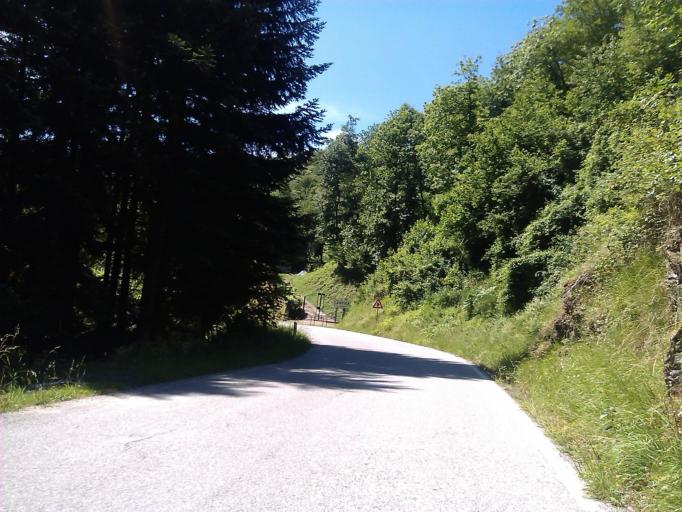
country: IT
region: Tuscany
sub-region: Provincia di Pistoia
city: Sambuca Pistoiese
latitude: 44.0834
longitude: 11.0462
